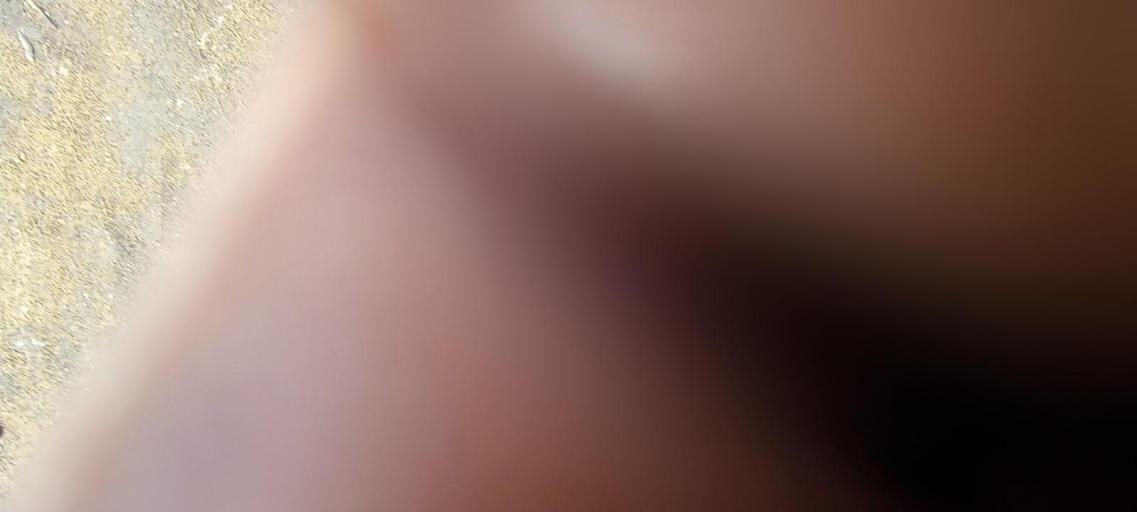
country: KE
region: Homa Bay
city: Homa Bay
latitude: -0.4568
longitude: 34.1933
